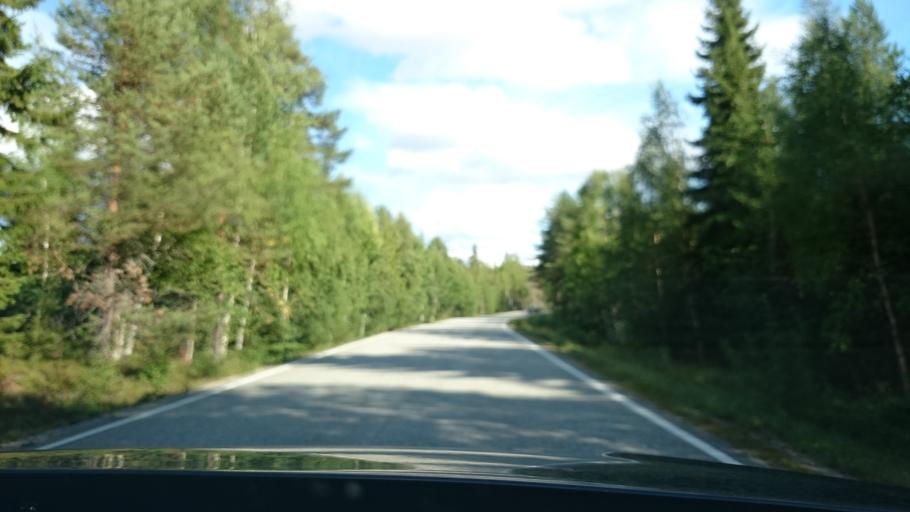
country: FI
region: Kainuu
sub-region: Kehys-Kainuu
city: Suomussalmi
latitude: 64.7561
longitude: 29.4085
